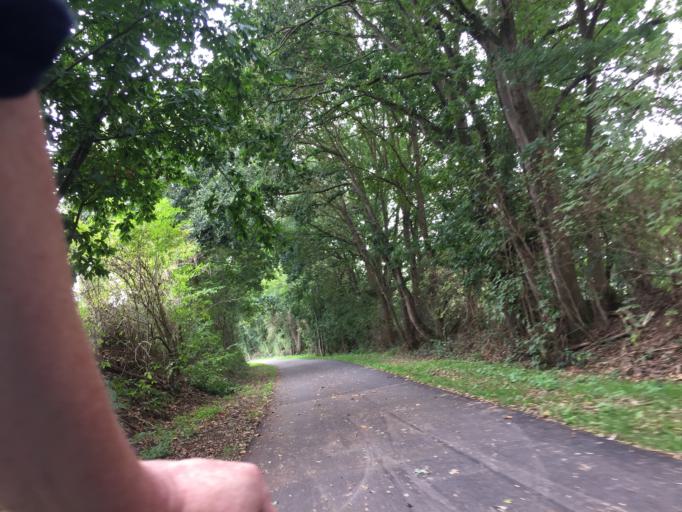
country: FR
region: Picardie
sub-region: Departement de l'Oise
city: Saint-Paul
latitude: 49.4119
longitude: 2.0122
